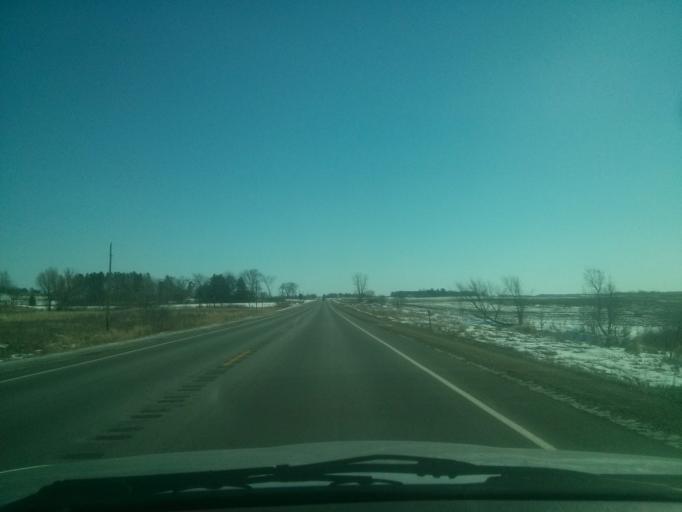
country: US
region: Wisconsin
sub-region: Polk County
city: Clear Lake
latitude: 45.1365
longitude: -92.3724
